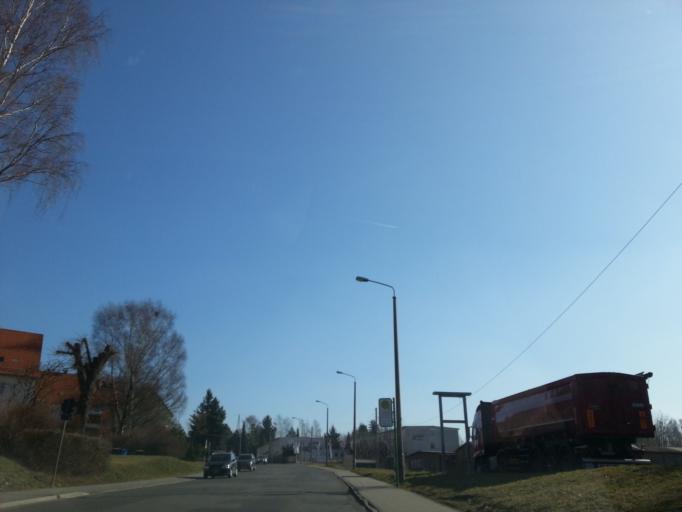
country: DE
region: Saxony
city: Freiberg
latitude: 50.9080
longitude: 13.3568
